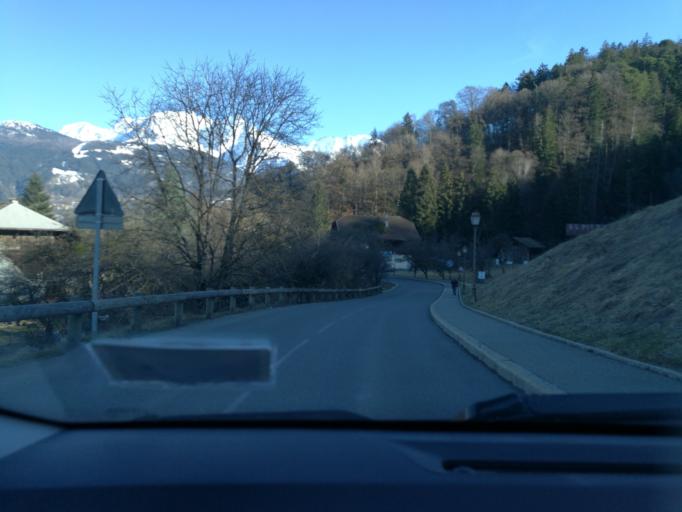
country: FR
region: Rhone-Alpes
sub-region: Departement de la Haute-Savoie
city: Domancy
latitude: 45.9110
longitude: 6.6524
